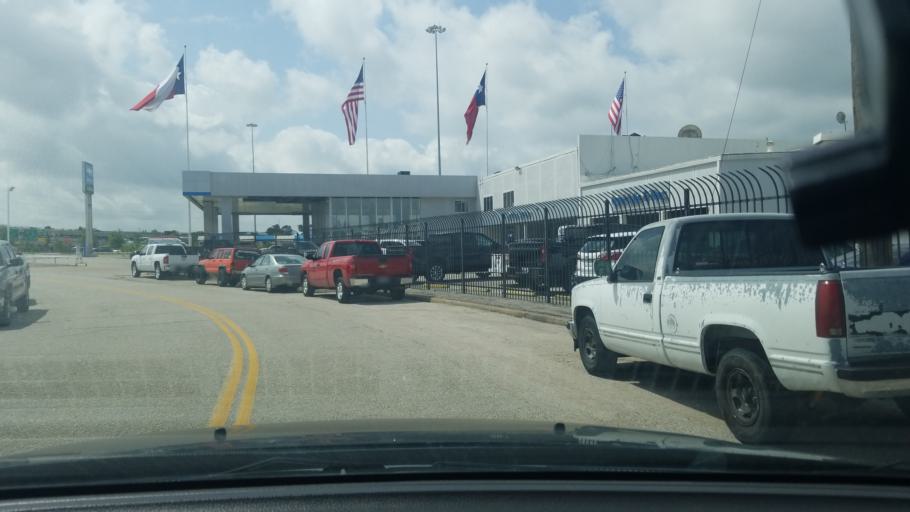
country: US
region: Texas
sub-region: Dallas County
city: Mesquite
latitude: 32.7992
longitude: -96.6852
